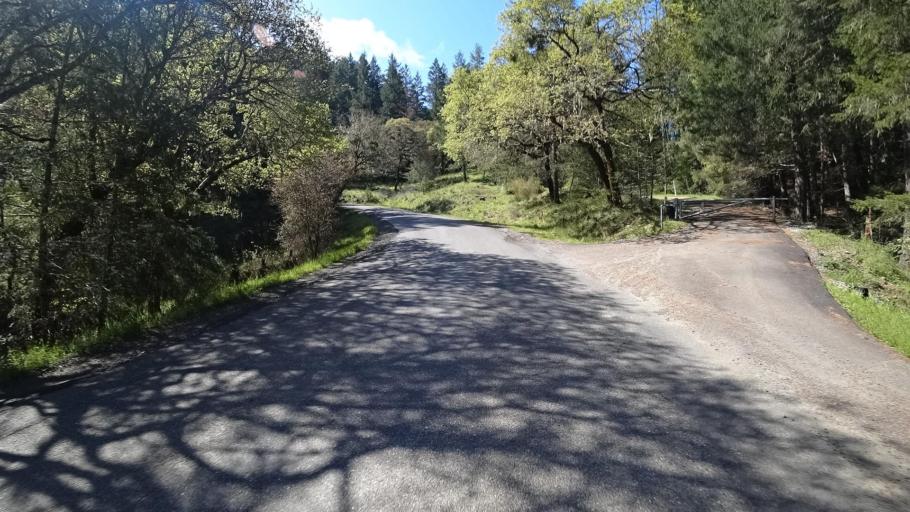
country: US
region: California
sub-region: Humboldt County
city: Redway
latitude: 40.0453
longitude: -123.6426
